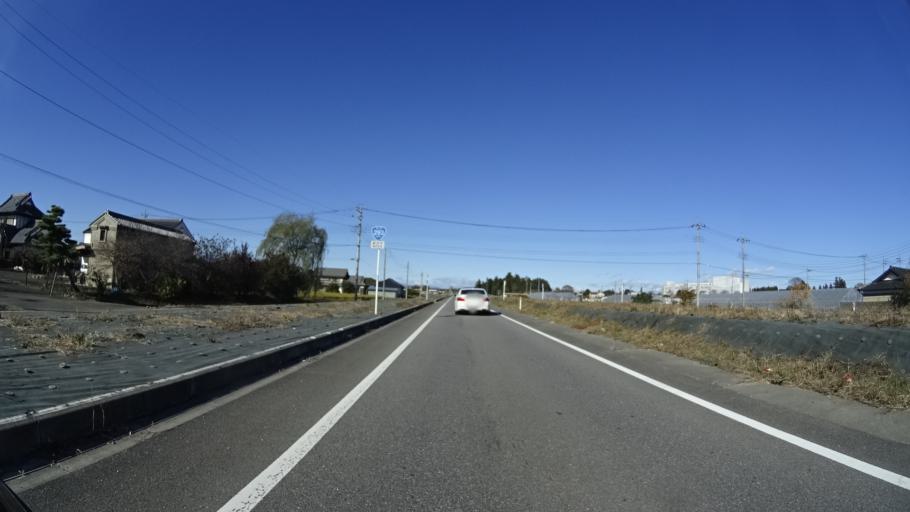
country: JP
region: Tochigi
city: Kanuma
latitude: 36.4833
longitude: 139.7536
